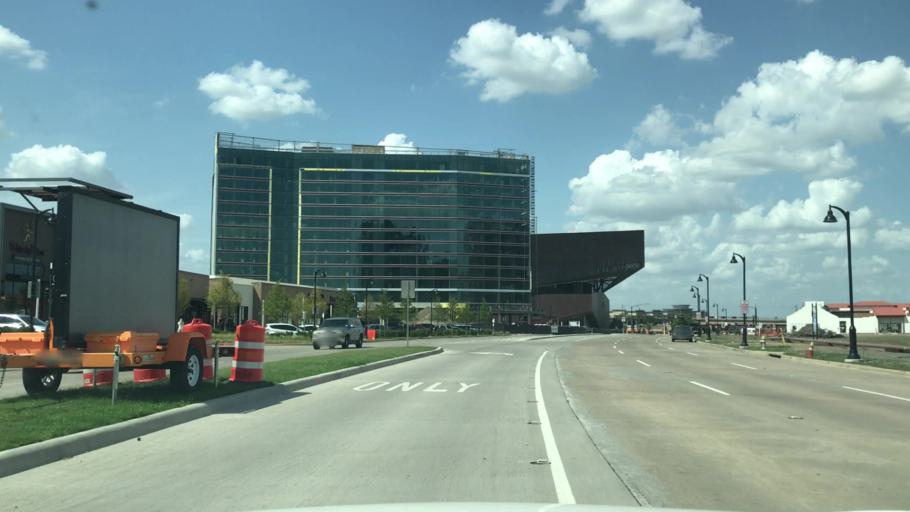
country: US
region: Texas
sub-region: Dallas County
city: Irving
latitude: 32.8747
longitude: -96.9436
